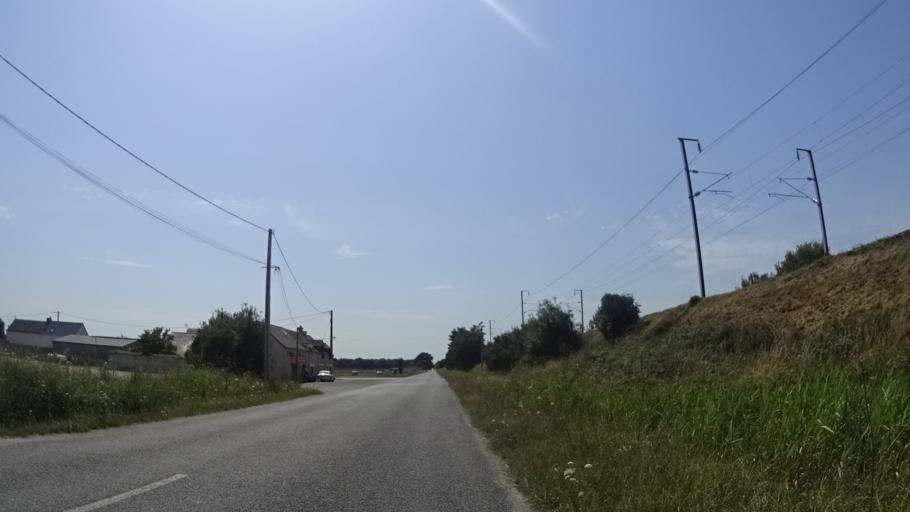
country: FR
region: Pays de la Loire
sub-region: Departement de la Loire-Atlantique
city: La Chapelle-Launay
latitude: 47.3581
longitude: -1.9747
